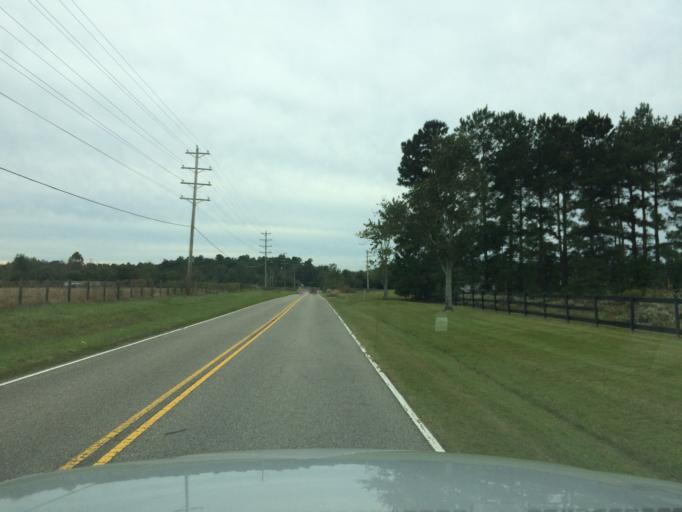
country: US
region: South Carolina
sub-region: Aiken County
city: New Ellenton
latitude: 33.3992
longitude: -81.7020
